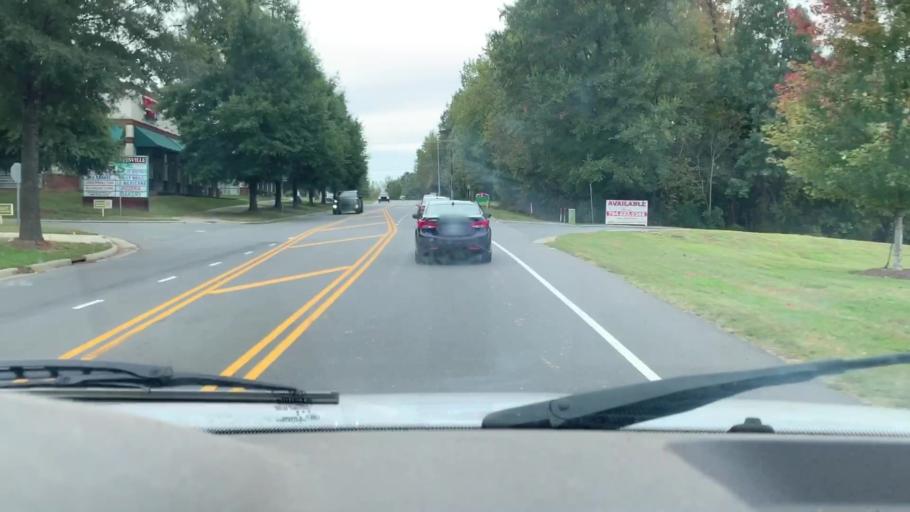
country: US
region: North Carolina
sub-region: Mecklenburg County
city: Huntersville
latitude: 35.4376
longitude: -80.8654
